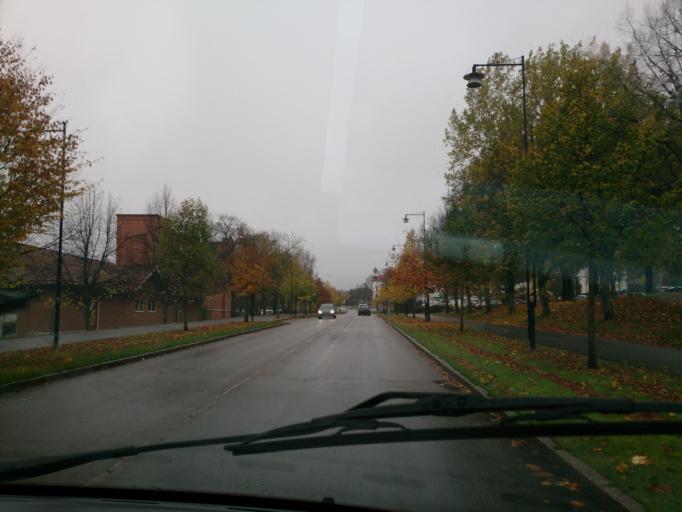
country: SE
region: OEstergoetland
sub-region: Atvidabergs Kommun
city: Atvidaberg
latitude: 58.2017
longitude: 16.0008
